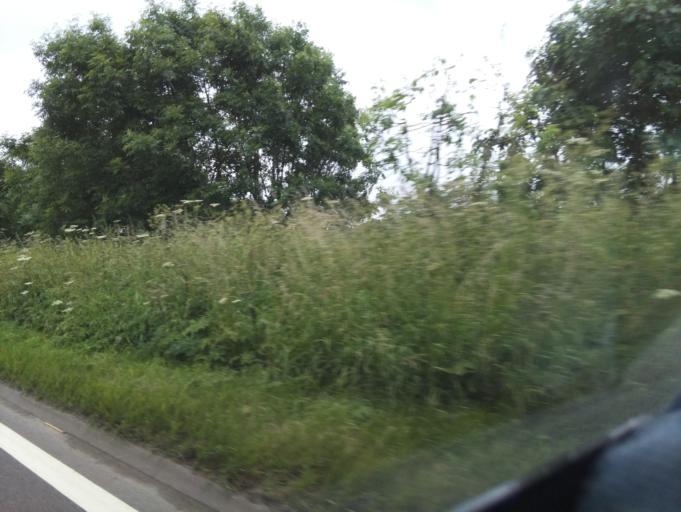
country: GB
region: England
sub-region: Derbyshire
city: Yeldersley
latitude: 52.9647
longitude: -1.6049
